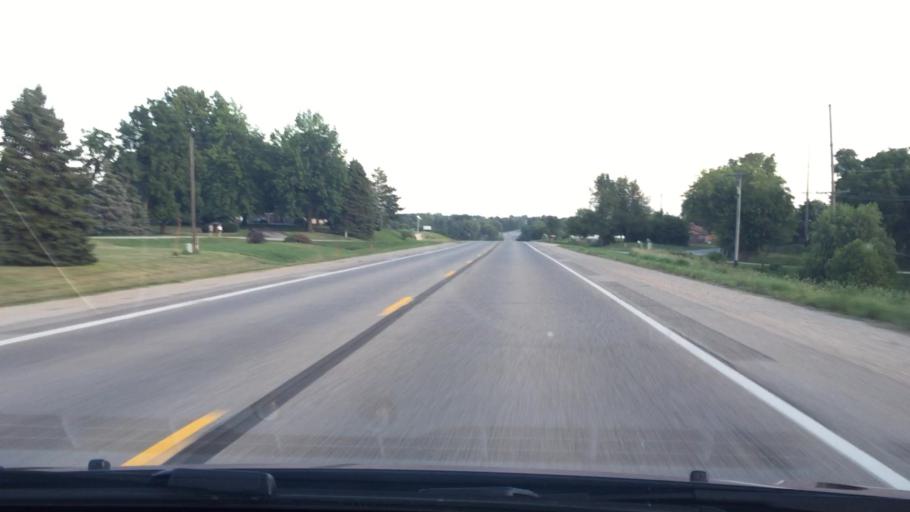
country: US
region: Iowa
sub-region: Muscatine County
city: Muscatine
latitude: 41.4690
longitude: -91.0360
